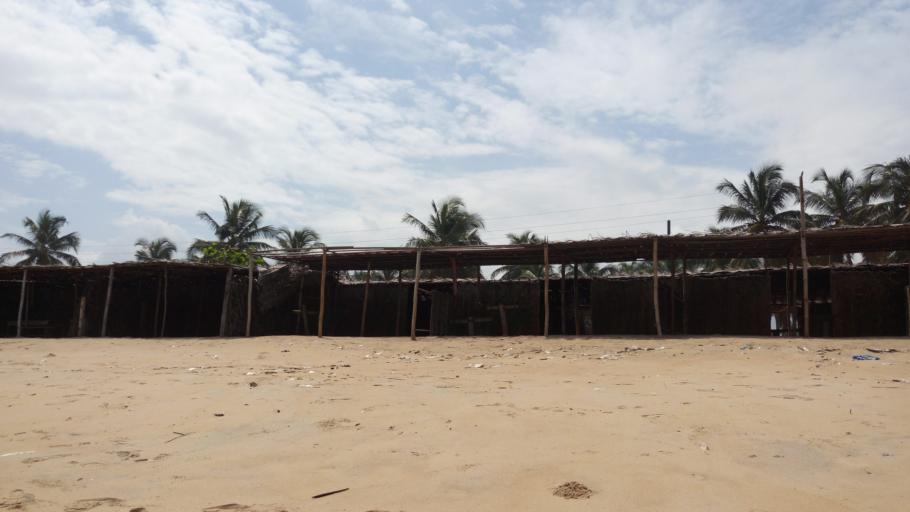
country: CI
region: Sud-Comoe
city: Grand-Bassam
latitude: 5.1865
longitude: -3.6863
